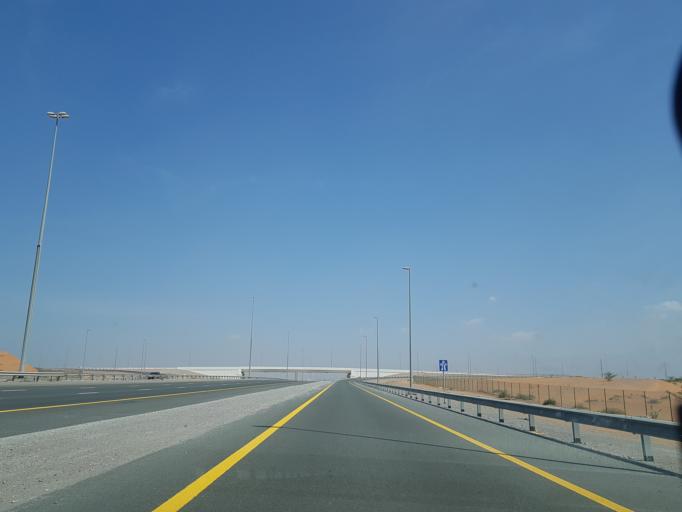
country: AE
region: Ra's al Khaymah
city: Ras al-Khaimah
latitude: 25.6928
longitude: 55.9225
